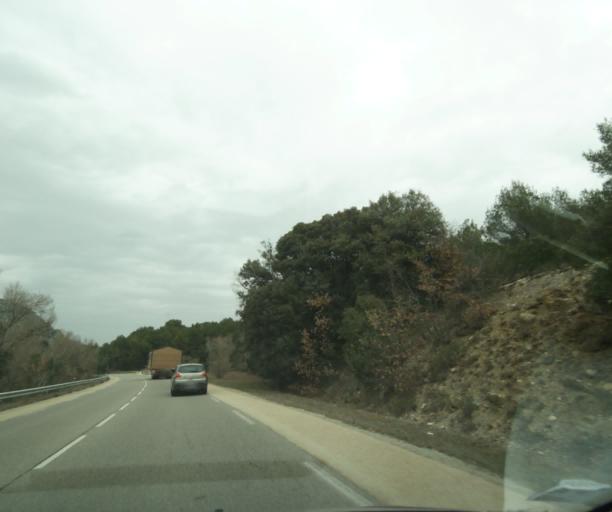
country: FR
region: Provence-Alpes-Cote d'Azur
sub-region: Departement des Bouches-du-Rhone
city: Jouques
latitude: 43.6681
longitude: 5.6476
